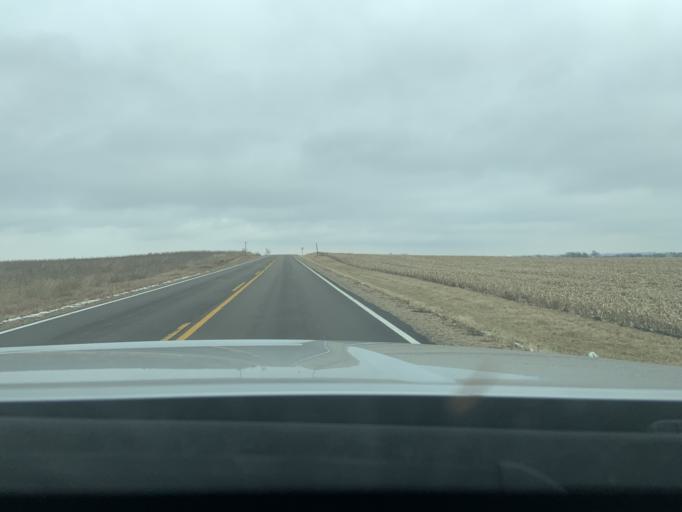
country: US
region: Illinois
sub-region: LaSalle County
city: Sheridan
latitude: 41.4580
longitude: -88.6154
